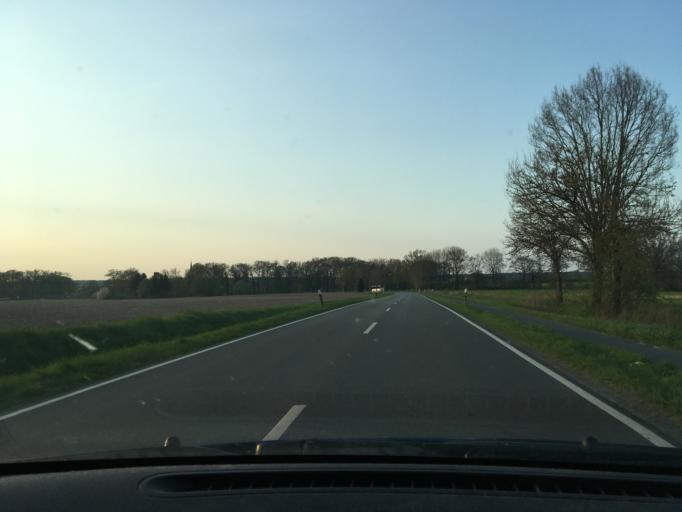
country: DE
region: Lower Saxony
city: Sudergellersen
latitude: 53.2236
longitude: 10.2973
